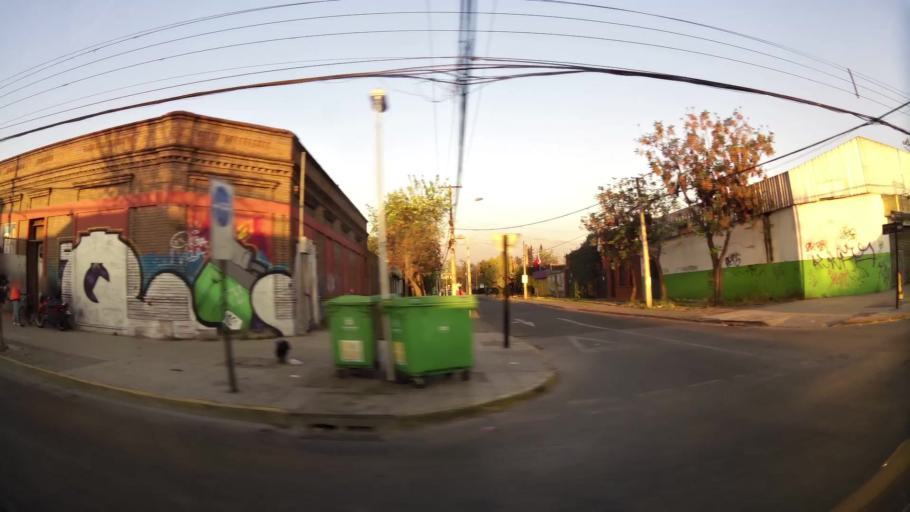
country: CL
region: Santiago Metropolitan
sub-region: Provincia de Santiago
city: Santiago
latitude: -33.4693
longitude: -70.6716
